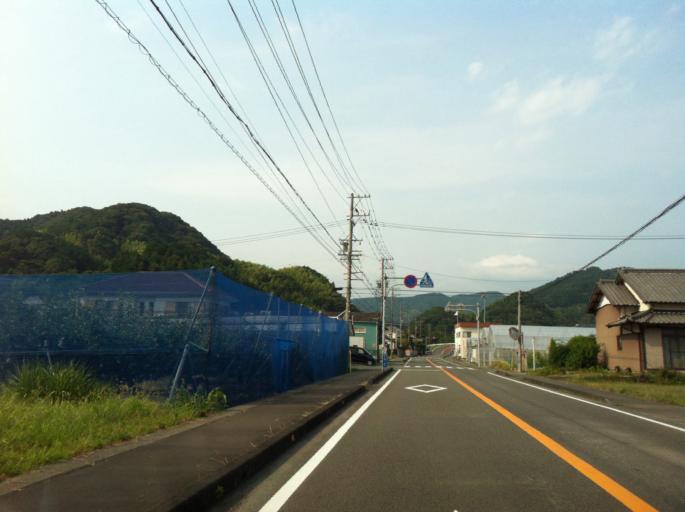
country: JP
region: Shizuoka
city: Fujieda
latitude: 34.9169
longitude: 138.2691
